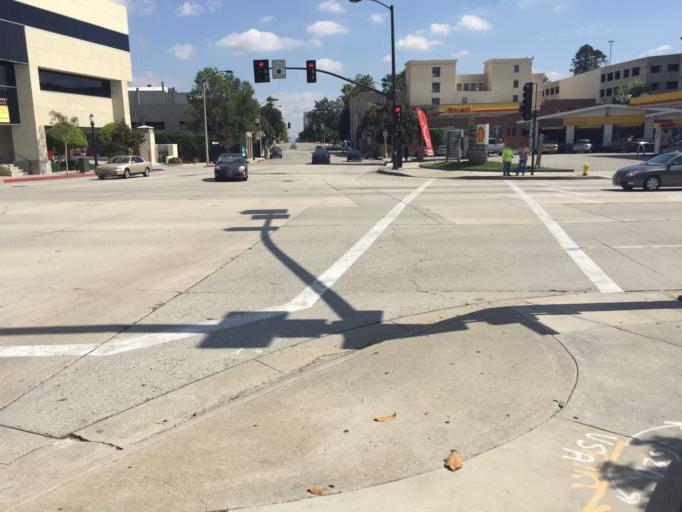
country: US
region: California
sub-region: Los Angeles County
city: Pasadena
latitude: 34.1495
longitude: -118.1507
